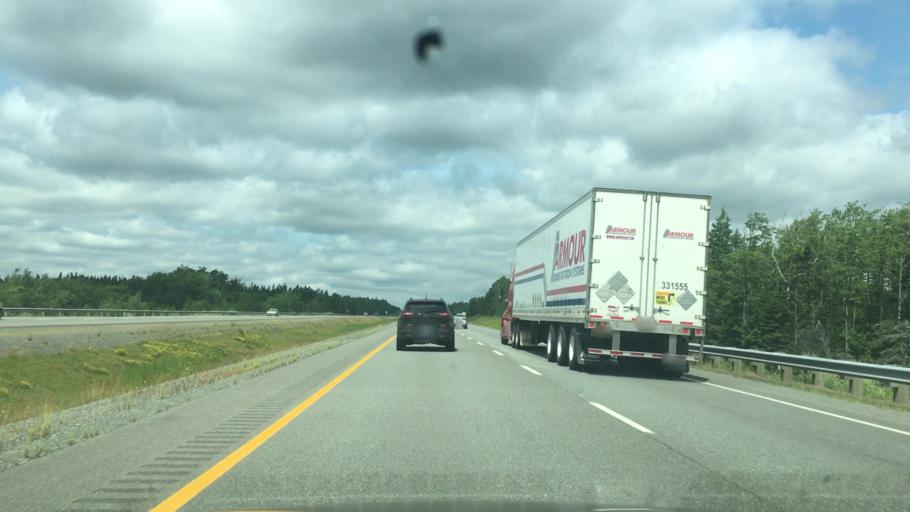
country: CA
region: Nova Scotia
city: Springhill
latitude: 45.7094
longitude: -64.0371
